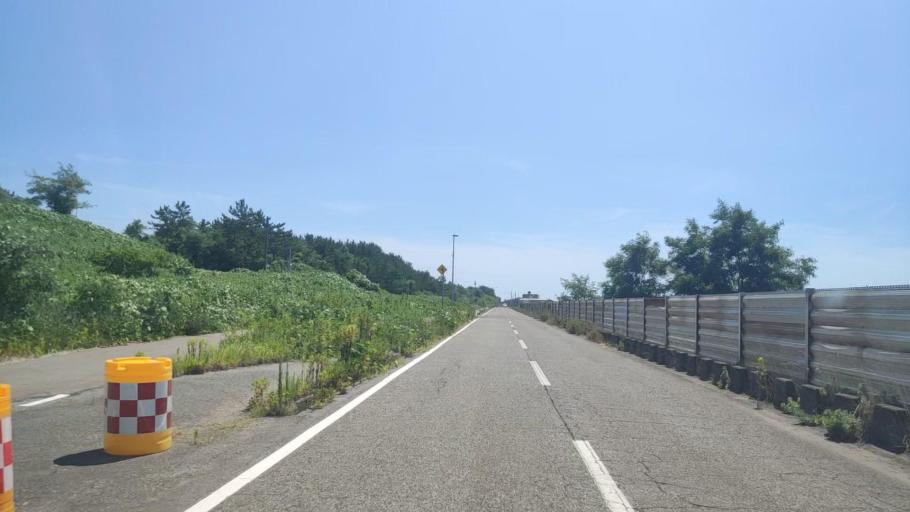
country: JP
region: Ishikawa
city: Kanazawa-shi
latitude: 36.6101
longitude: 136.5961
